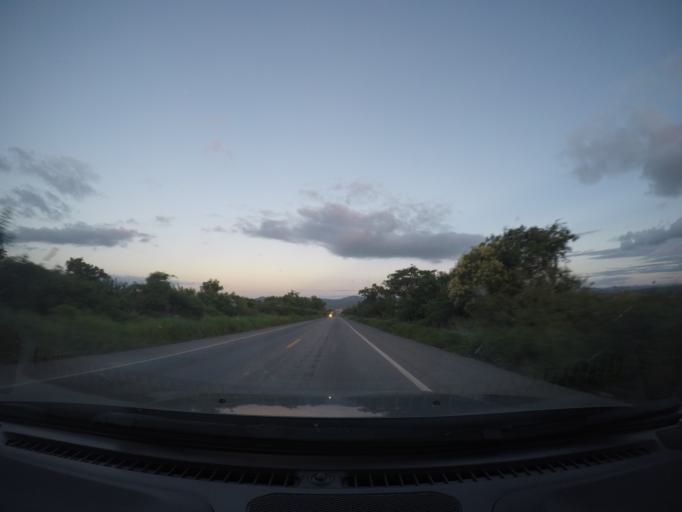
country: BR
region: Bahia
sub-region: Seabra
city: Seabra
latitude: -12.4306
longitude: -41.7940
